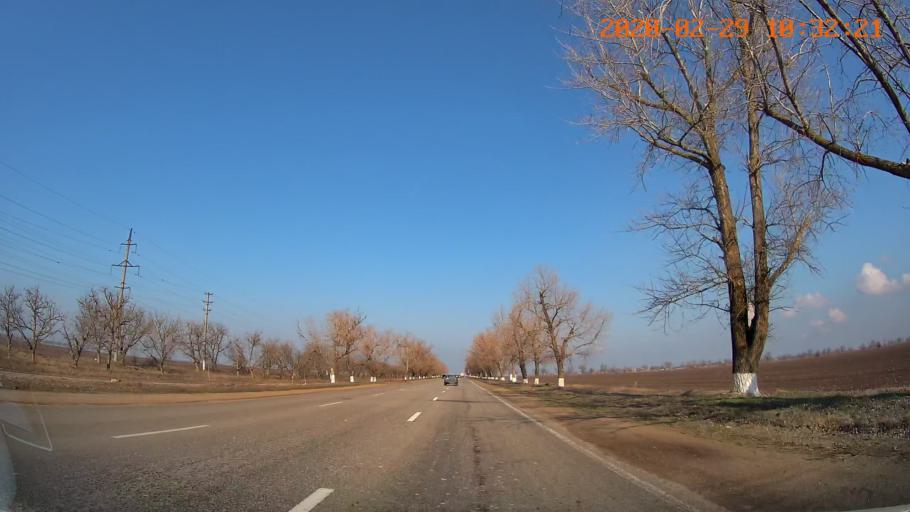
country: UA
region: Odessa
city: Velykoploske
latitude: 46.9599
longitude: 29.5546
